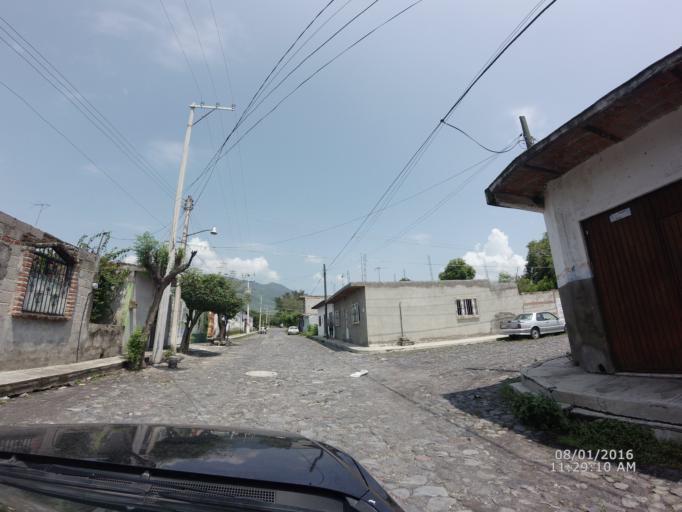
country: MX
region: Nayarit
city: Jala
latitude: 21.1071
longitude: -104.4453
